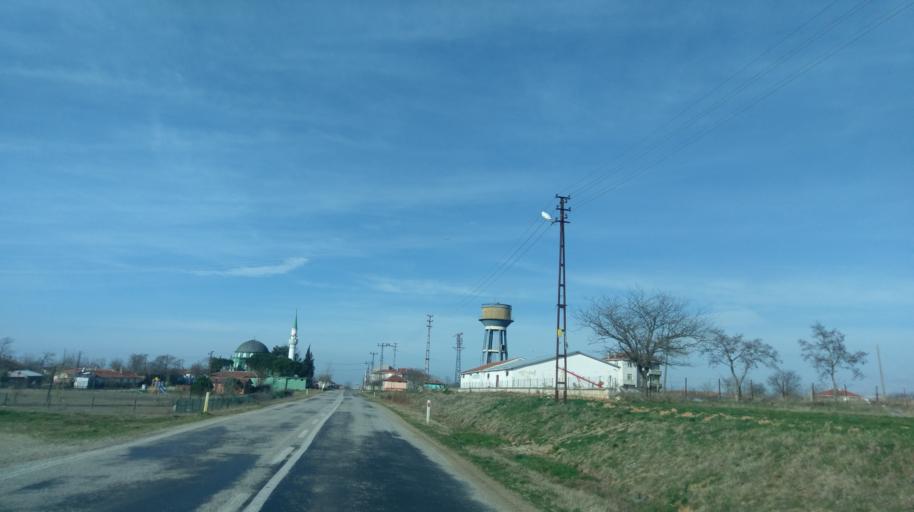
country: TR
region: Edirne
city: Copkoy
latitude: 41.3075
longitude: 26.8288
